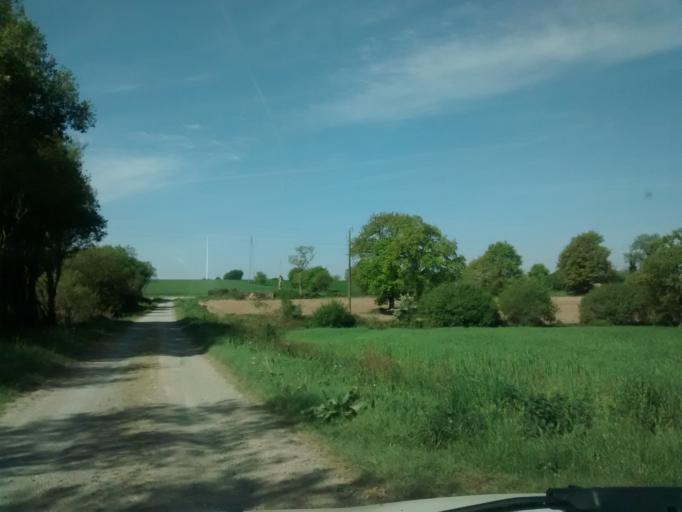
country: FR
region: Brittany
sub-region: Departement d'Ille-et-Vilaine
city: Grand-Fougeray
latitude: 47.7823
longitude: -1.7545
